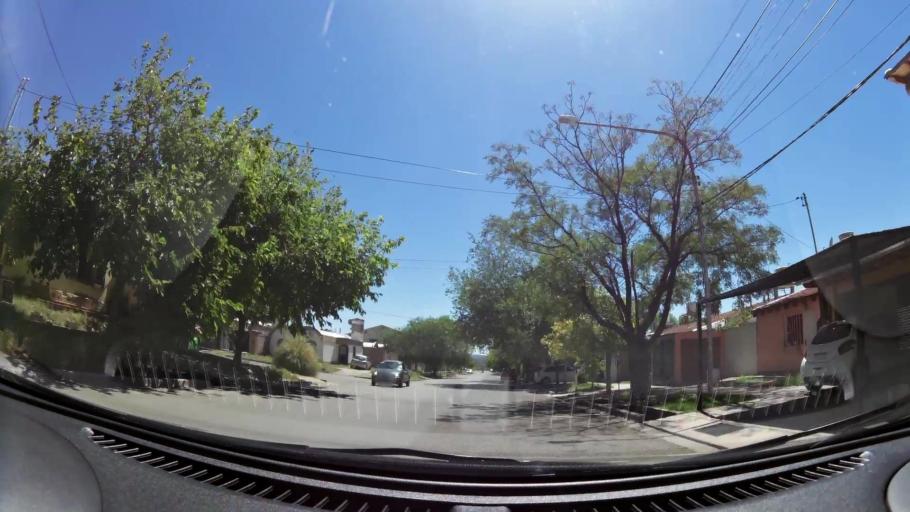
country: AR
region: Mendoza
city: Las Heras
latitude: -32.8374
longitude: -68.8687
